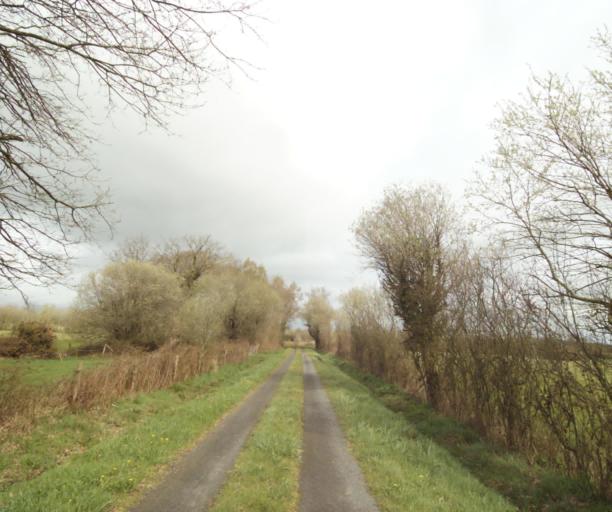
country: FR
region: Pays de la Loire
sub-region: Departement de la Loire-Atlantique
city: Bouvron
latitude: 47.4295
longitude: -1.8925
